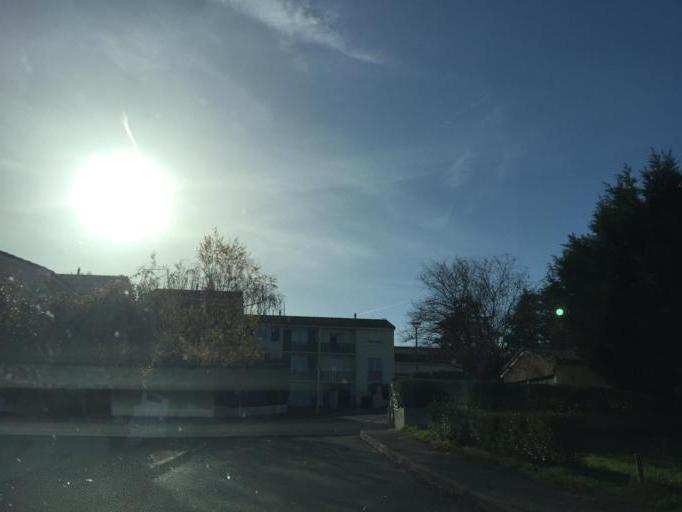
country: FR
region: Rhone-Alpes
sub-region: Departement de la Loire
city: Saint-Chamond
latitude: 45.4762
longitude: 4.5271
